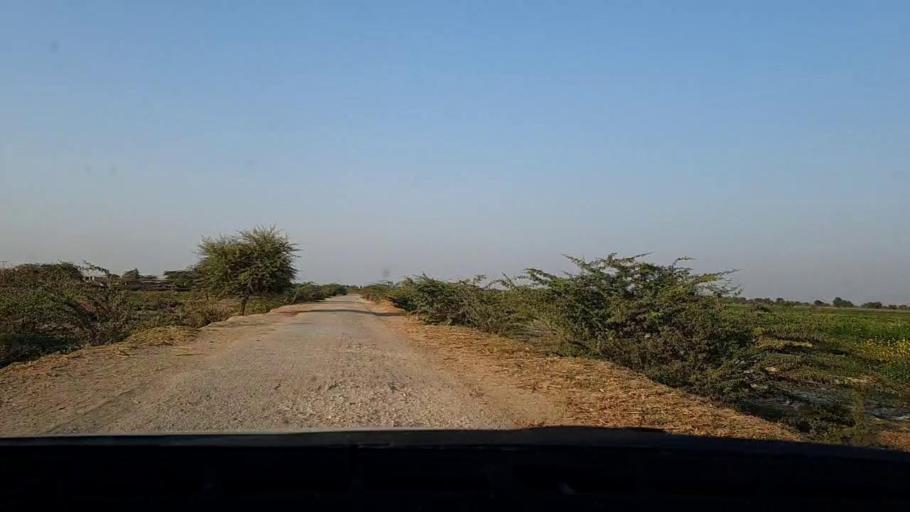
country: PK
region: Sindh
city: Tando Mittha Khan
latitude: 25.8623
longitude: 69.2726
